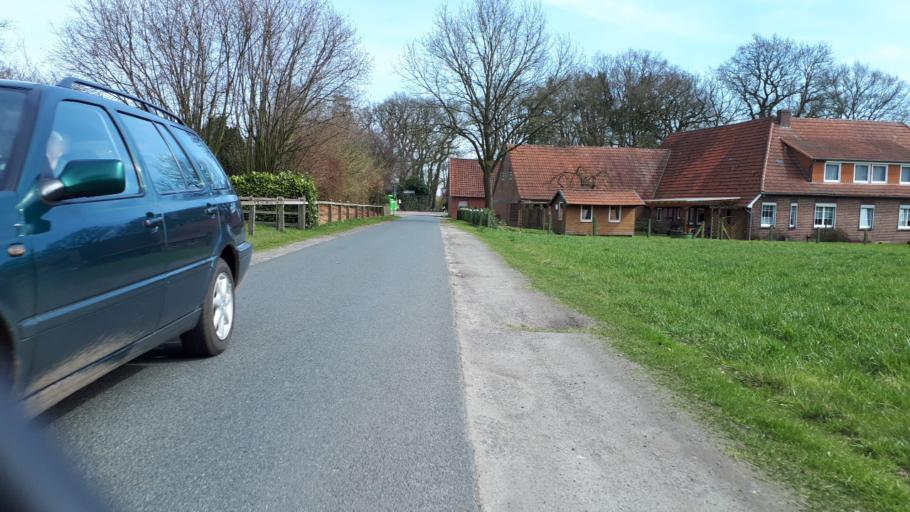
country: DE
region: Lower Saxony
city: Hatten
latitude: 53.0097
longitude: 8.3174
